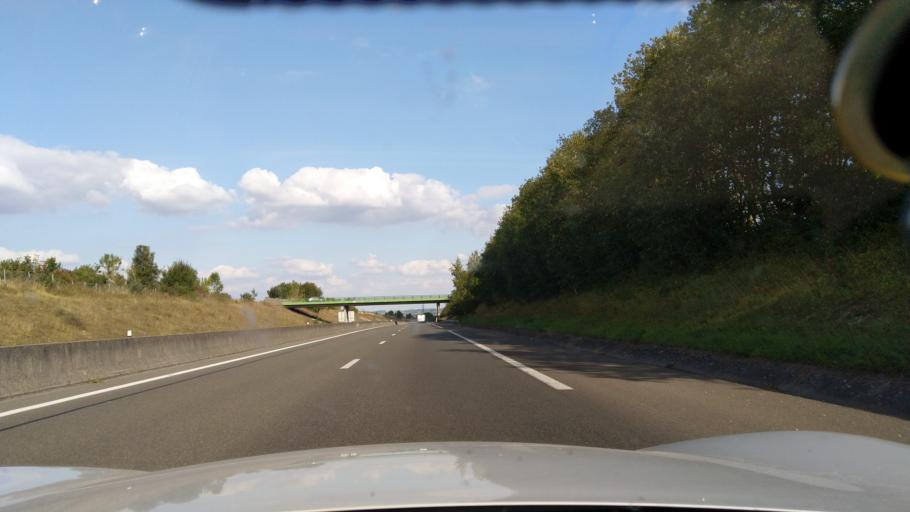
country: FR
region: Picardie
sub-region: Departement de la Somme
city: Flixecourt
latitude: 50.0327
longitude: 2.0616
